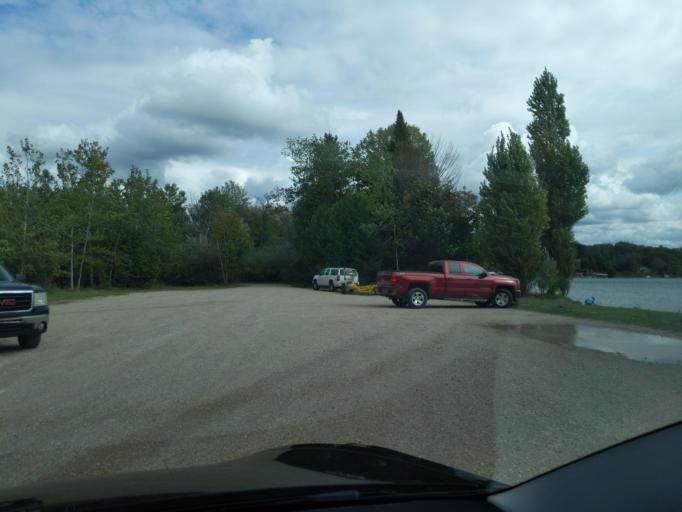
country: US
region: Michigan
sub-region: Antrim County
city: Bellaire
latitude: 45.1060
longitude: -85.3467
